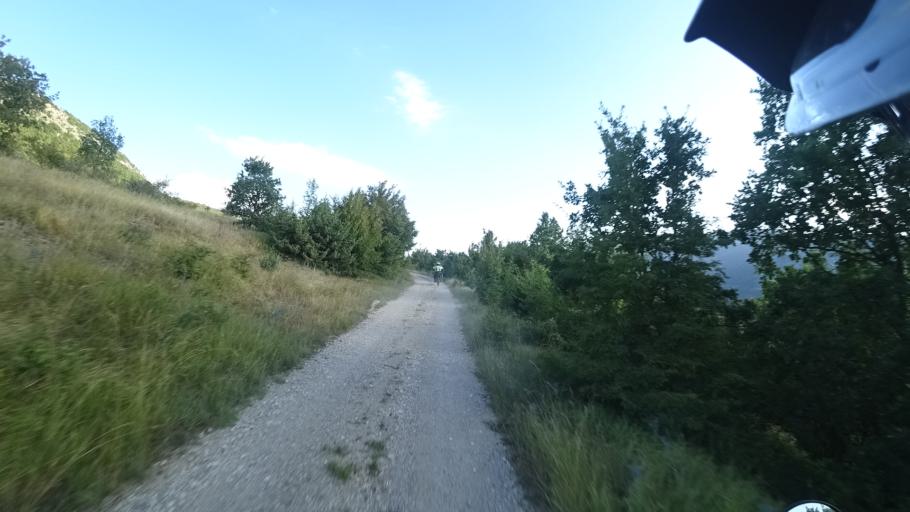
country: HR
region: Sibensko-Kniniska
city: Knin
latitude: 44.1751
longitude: 16.0703
